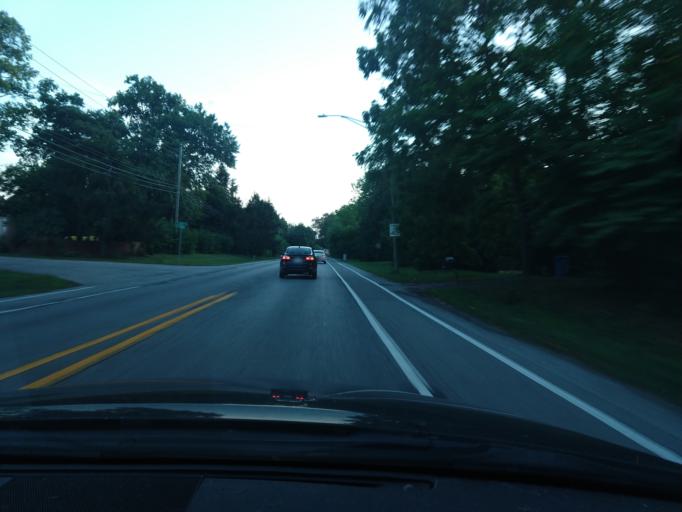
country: US
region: Indiana
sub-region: Marion County
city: Broad Ripple
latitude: 39.8610
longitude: -86.1007
